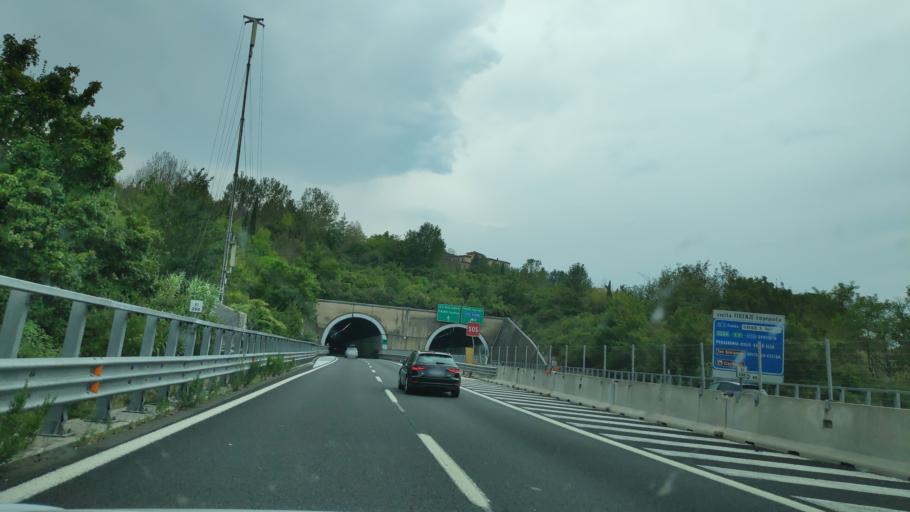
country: IT
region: Tuscany
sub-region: Province of Florence
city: Tavarnuzze
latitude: 43.7214
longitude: 11.2342
